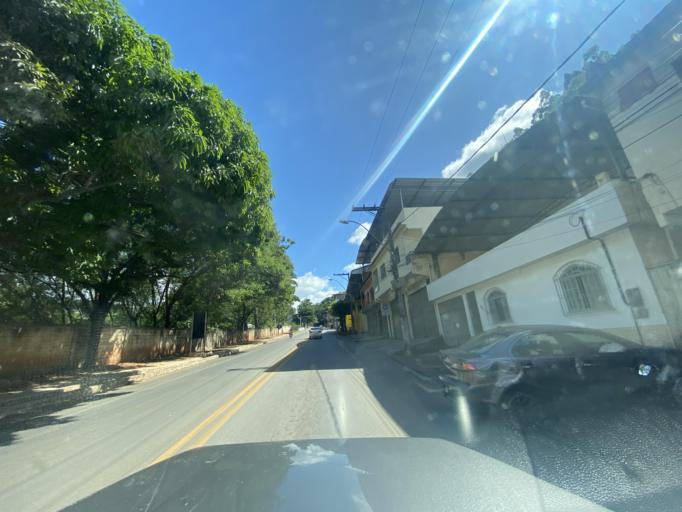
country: BR
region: Espirito Santo
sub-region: Alegre
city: Alegre
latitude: -20.7622
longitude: -41.5247
